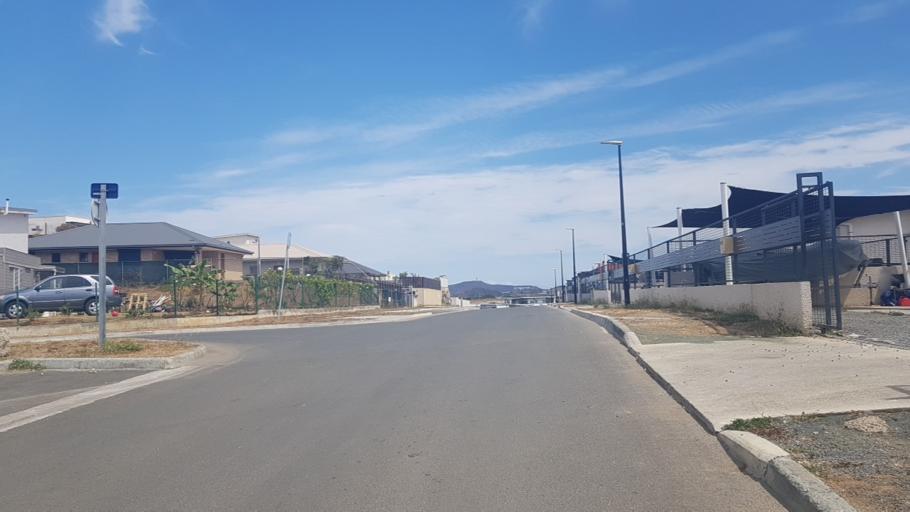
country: NC
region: South Province
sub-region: Dumbea
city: Dumbea
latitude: -22.2003
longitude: 166.4436
